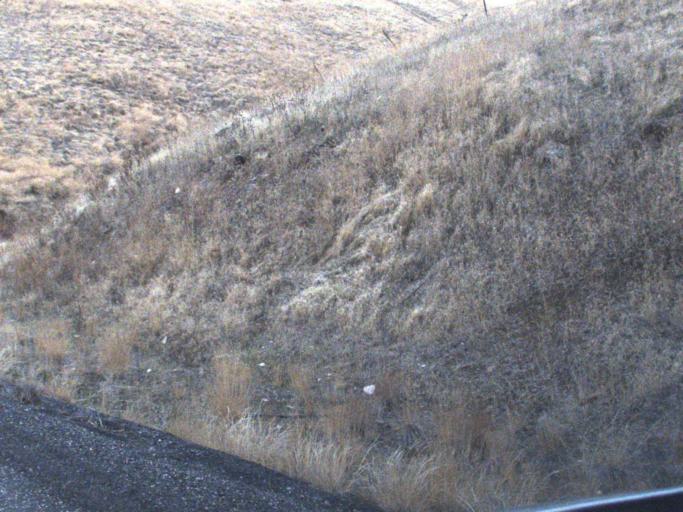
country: US
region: Washington
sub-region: Garfield County
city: Pomeroy
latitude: 46.4420
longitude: -117.3837
